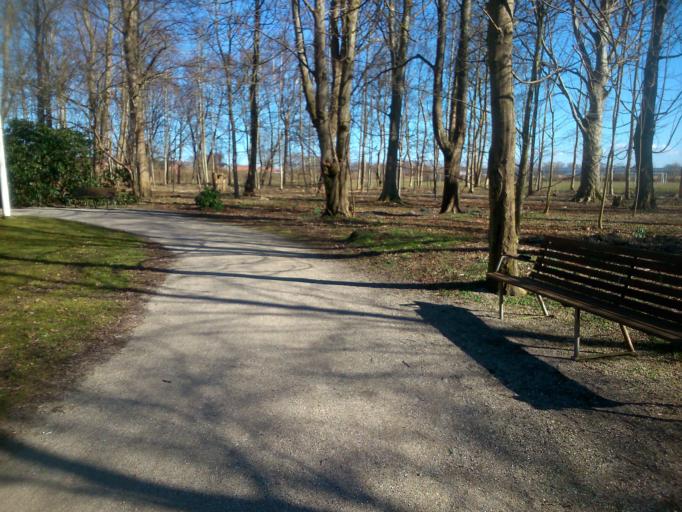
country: DK
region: Central Jutland
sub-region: Ringkobing-Skjern Kommune
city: Ringkobing
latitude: 56.0854
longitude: 8.2625
